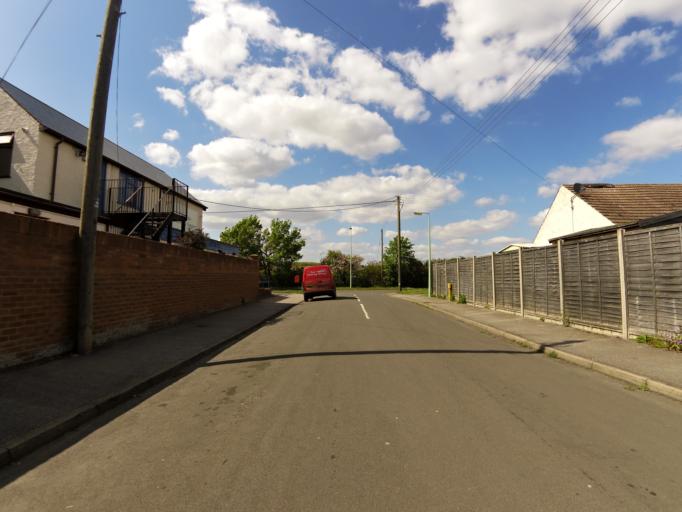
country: GB
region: England
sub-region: Suffolk
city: Kessingland
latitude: 52.4522
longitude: 1.7025
